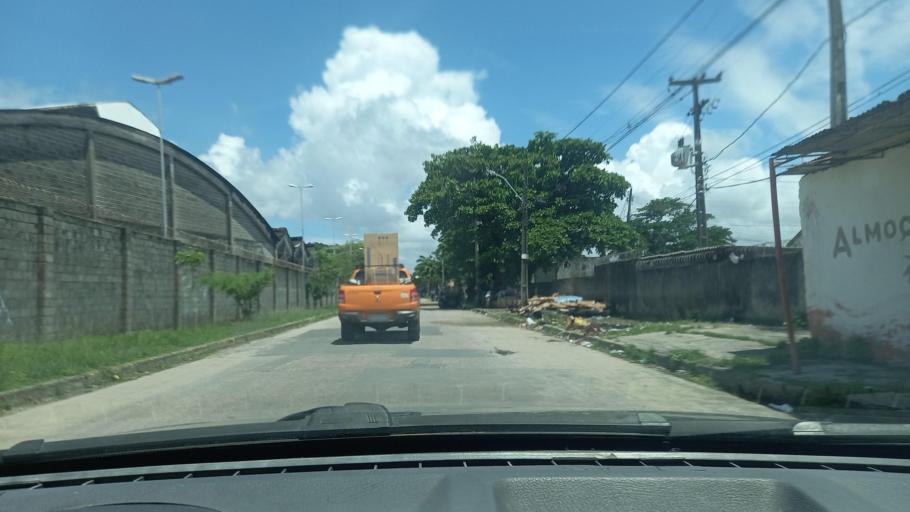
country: BR
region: Pernambuco
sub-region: Recife
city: Recife
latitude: -8.1028
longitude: -34.9091
